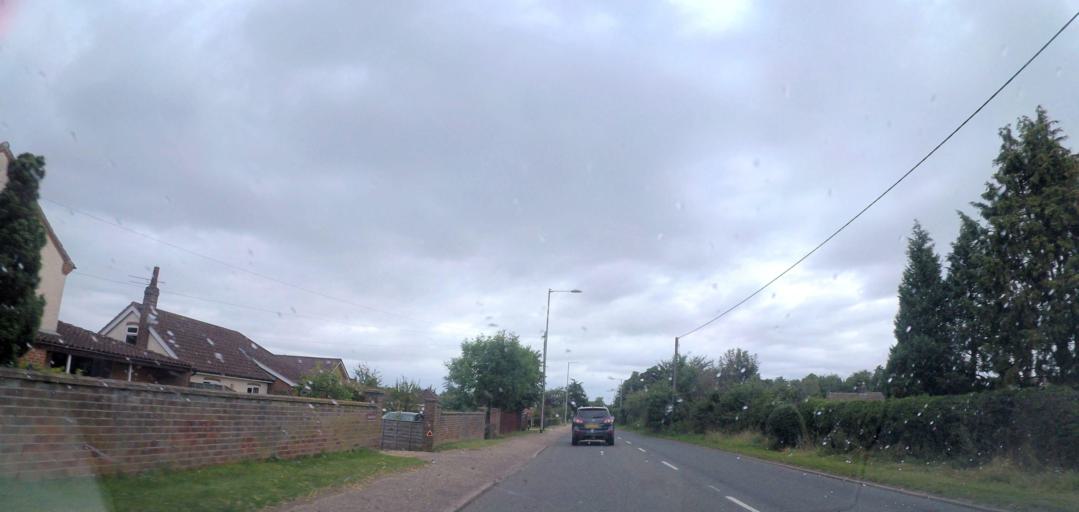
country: GB
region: England
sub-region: Norfolk
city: Coltishall
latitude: 52.7213
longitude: 1.3504
